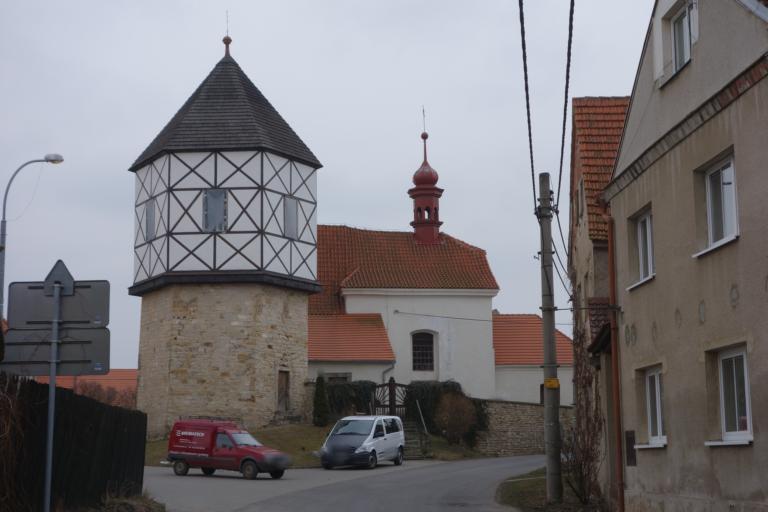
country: CZ
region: Ustecky
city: Polepy
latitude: 50.4782
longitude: 14.2392
